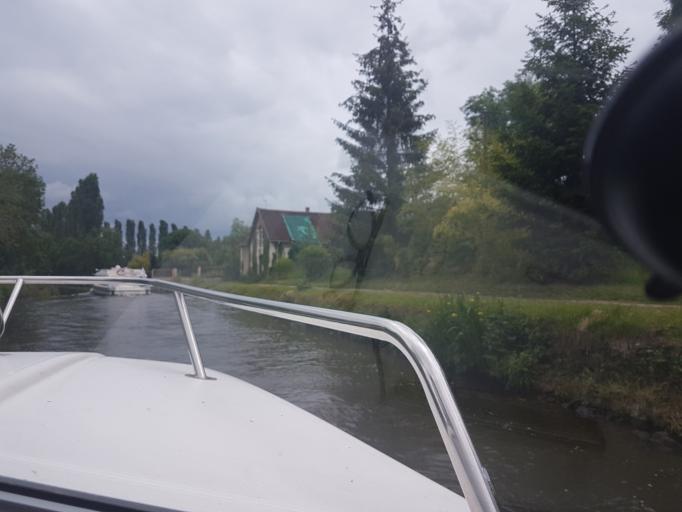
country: FR
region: Bourgogne
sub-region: Departement de l'Yonne
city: Champs-sur-Yonne
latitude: 47.7388
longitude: 3.5912
